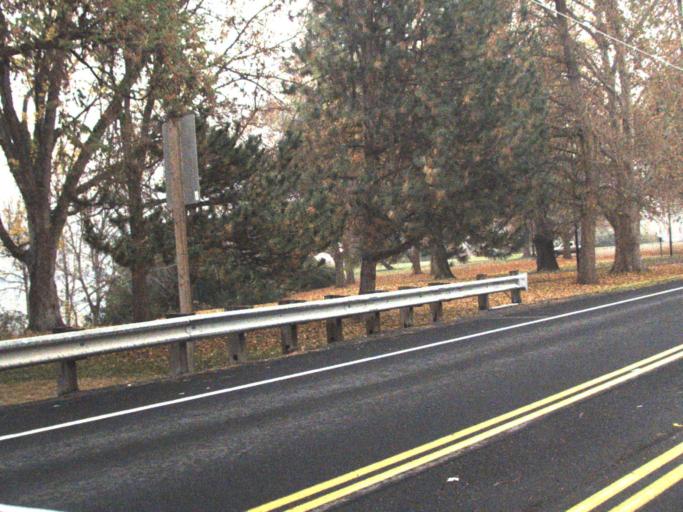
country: US
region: Washington
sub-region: Asotin County
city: West Clarkston-Highland
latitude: 46.3924
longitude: -117.0457
